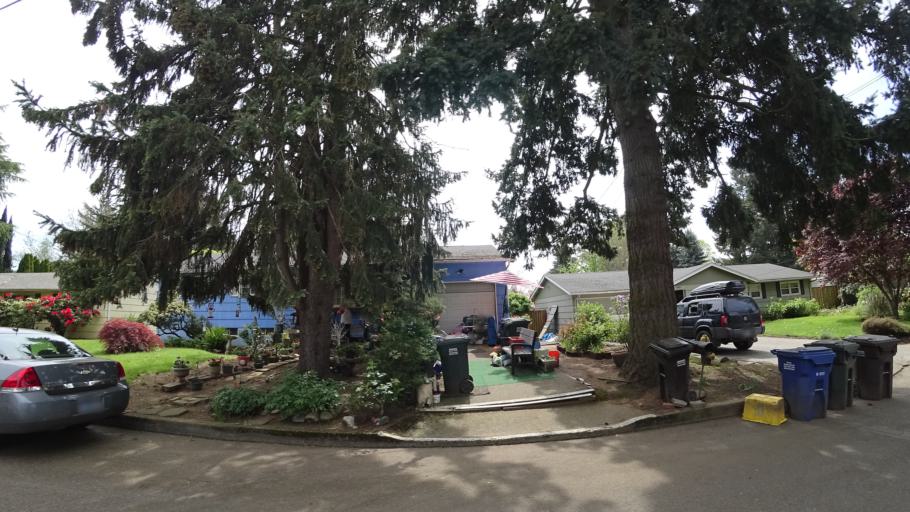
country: US
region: Oregon
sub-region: Clackamas County
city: Milwaukie
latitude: 45.4568
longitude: -122.6210
